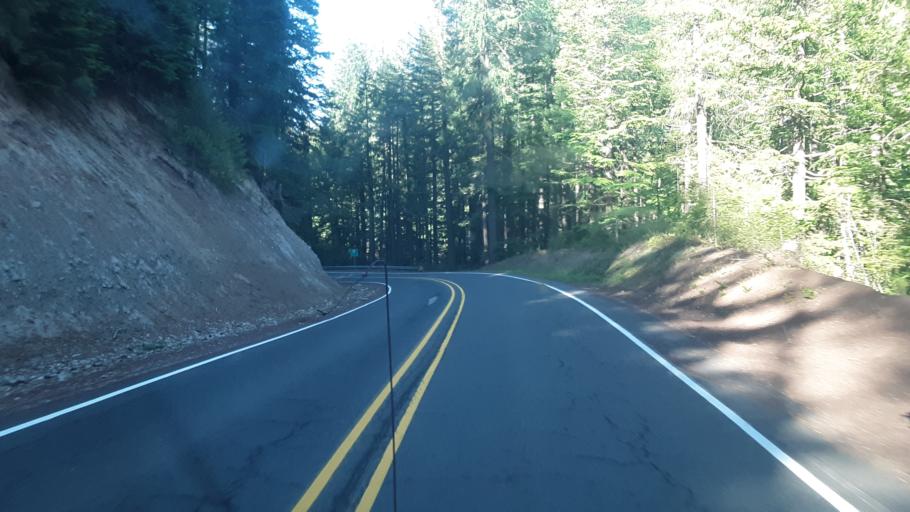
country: US
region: Oregon
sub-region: Jackson County
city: Shady Cove
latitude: 42.9254
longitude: -122.4265
